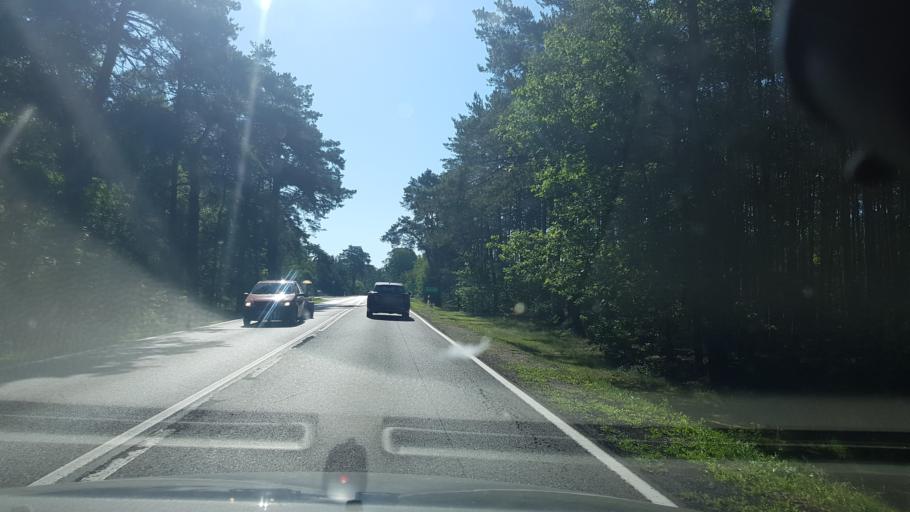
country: PL
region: Masovian Voivodeship
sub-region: Powiat wyszkowski
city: Branszczyk
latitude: 52.5574
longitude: 21.5856
